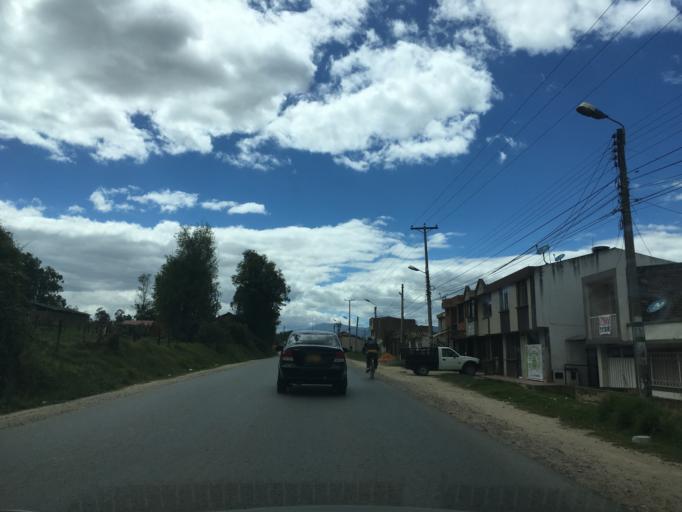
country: CO
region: Boyaca
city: Sogamoso
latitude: 5.6853
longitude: -72.9506
